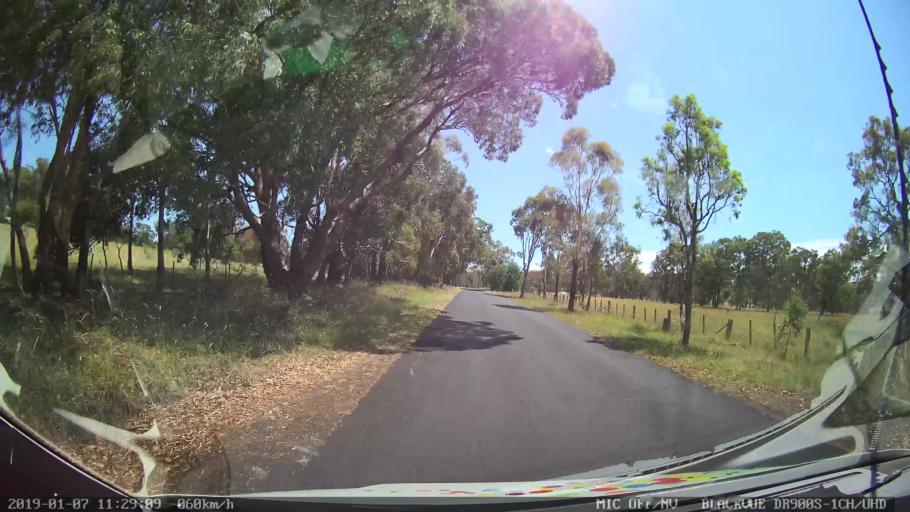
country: AU
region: New South Wales
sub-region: Armidale Dumaresq
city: Armidale
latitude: -30.4415
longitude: 151.5649
